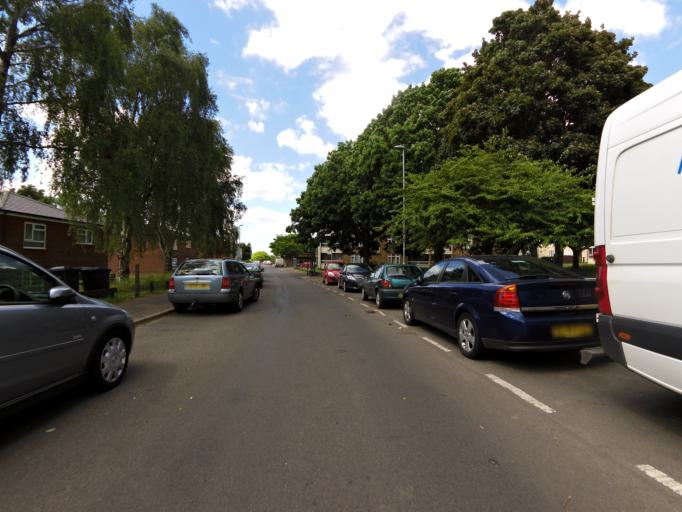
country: GB
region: England
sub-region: Norfolk
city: Norwich
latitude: 52.6513
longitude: 1.2699
